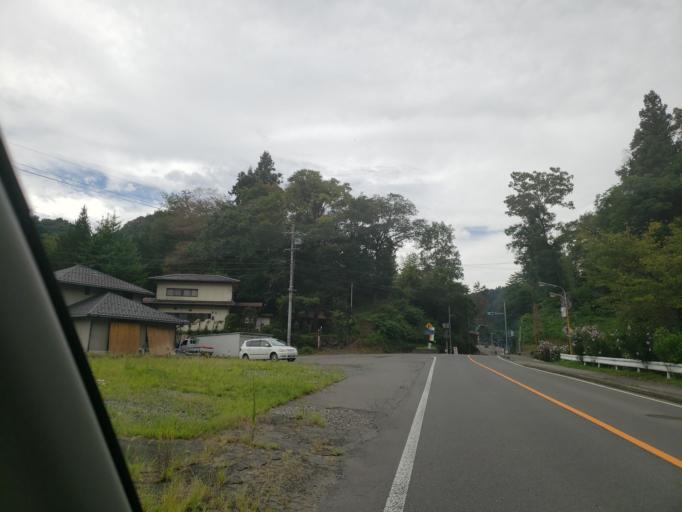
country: JP
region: Nagano
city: Nagano-shi
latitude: 36.6114
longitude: 138.0366
